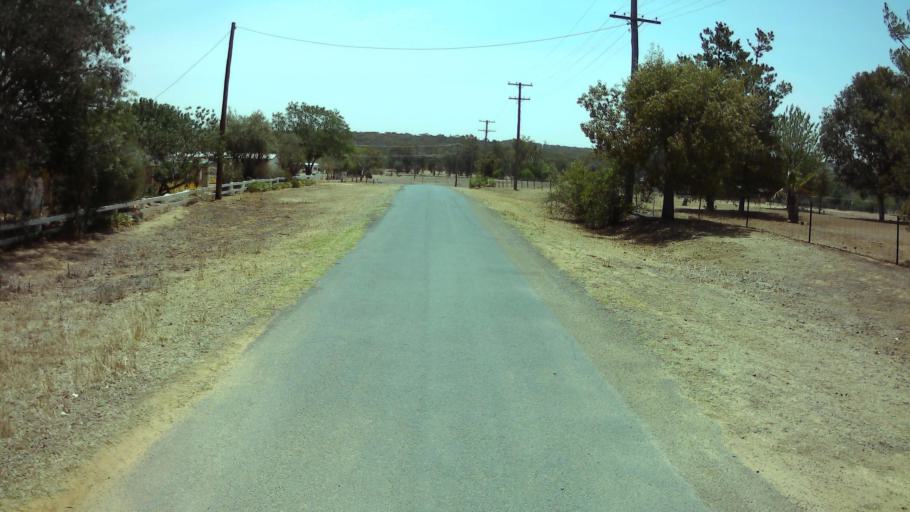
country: AU
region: New South Wales
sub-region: Weddin
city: Grenfell
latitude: -33.8937
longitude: 148.1723
